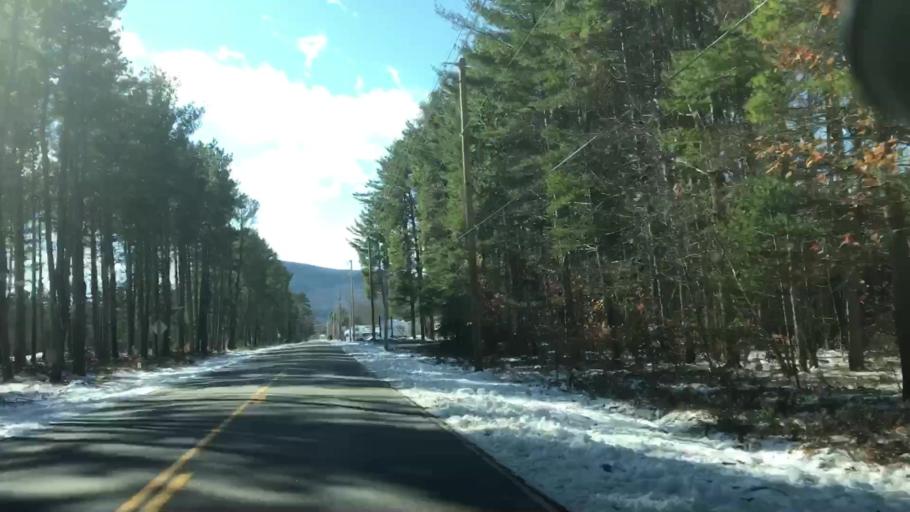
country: US
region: Maine
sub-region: Oxford County
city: Brownfield
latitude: 43.9536
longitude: -70.8836
